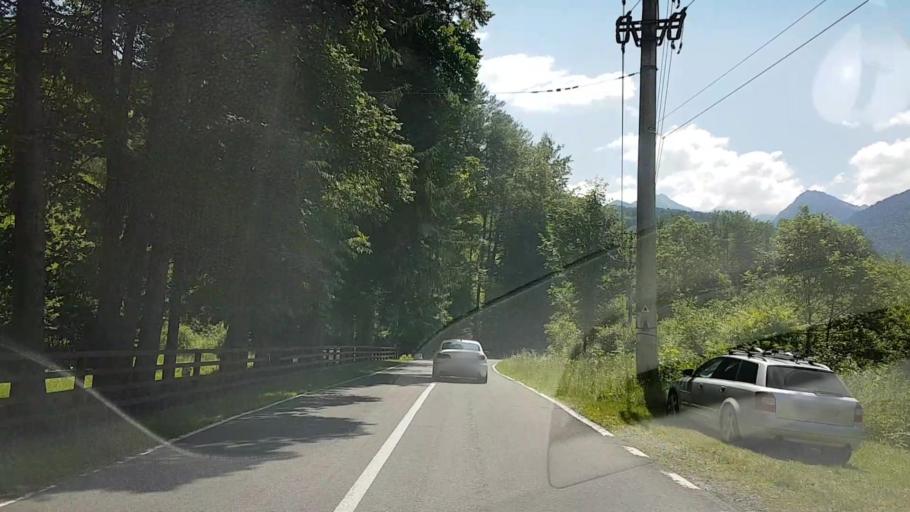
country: RO
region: Sibiu
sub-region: Comuna Cartisoara
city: Cartisoara
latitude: 45.6831
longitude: 24.5755
